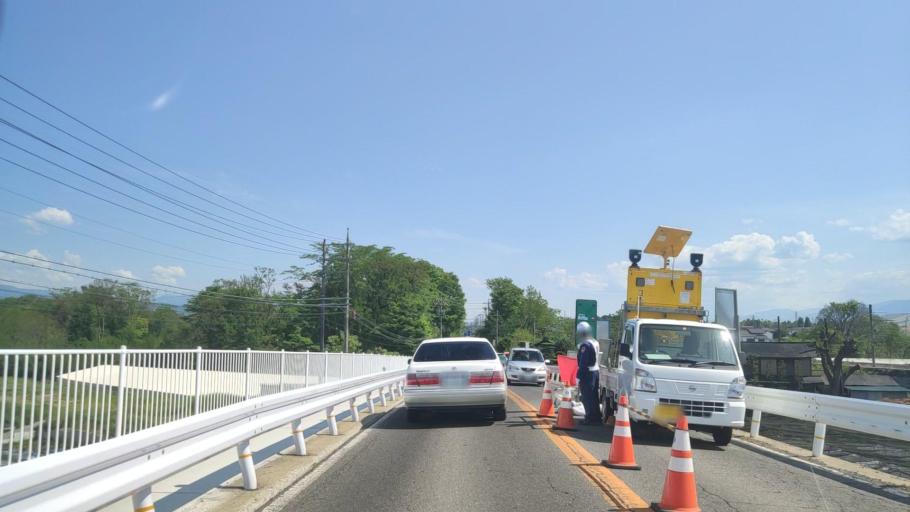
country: JP
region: Nagano
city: Hotaka
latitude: 36.3509
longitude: 137.8824
